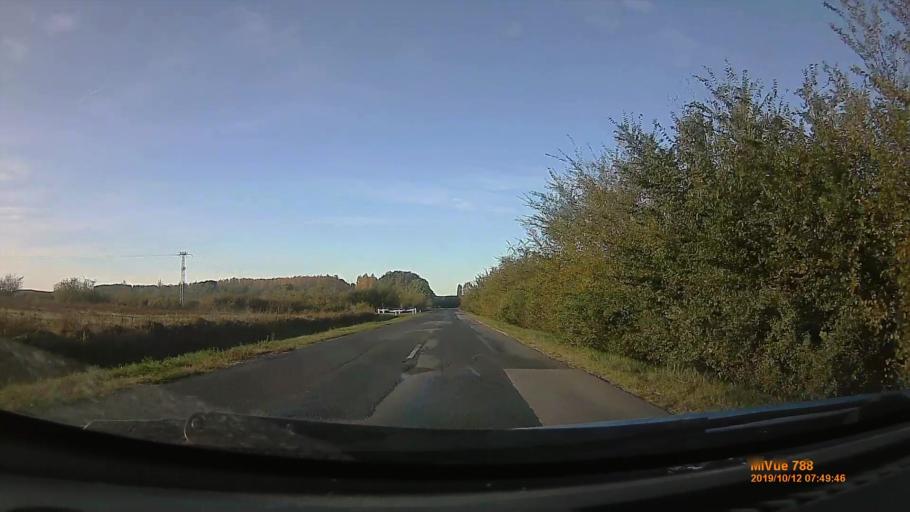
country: HU
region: Hajdu-Bihar
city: Biharkeresztes
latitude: 47.1594
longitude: 21.7426
